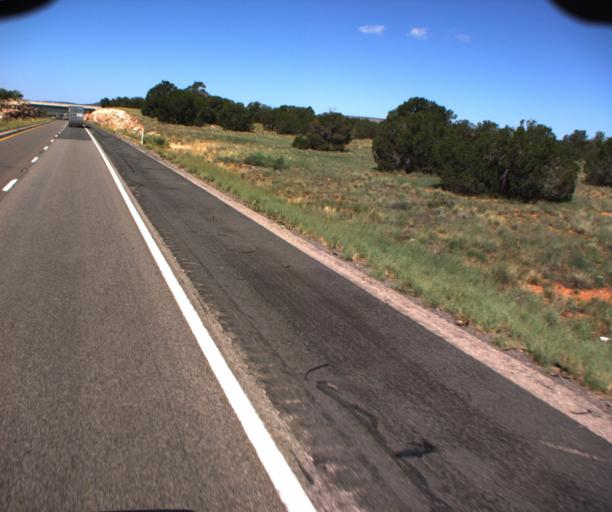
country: US
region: Arizona
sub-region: Mohave County
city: Peach Springs
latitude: 35.3207
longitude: -112.9459
